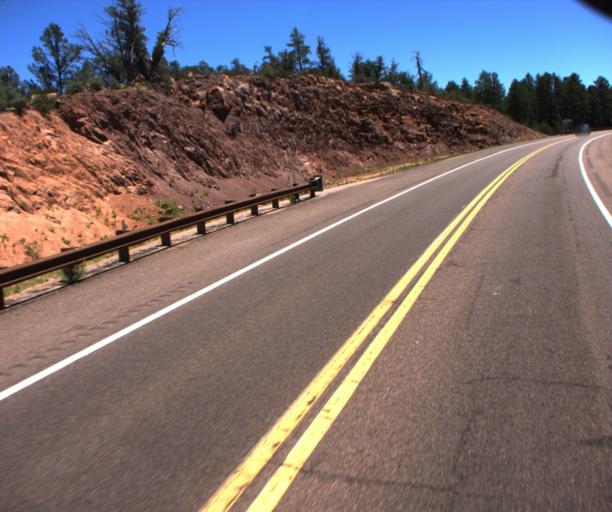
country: US
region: Arizona
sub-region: Gila County
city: Payson
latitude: 34.2766
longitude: -111.3221
